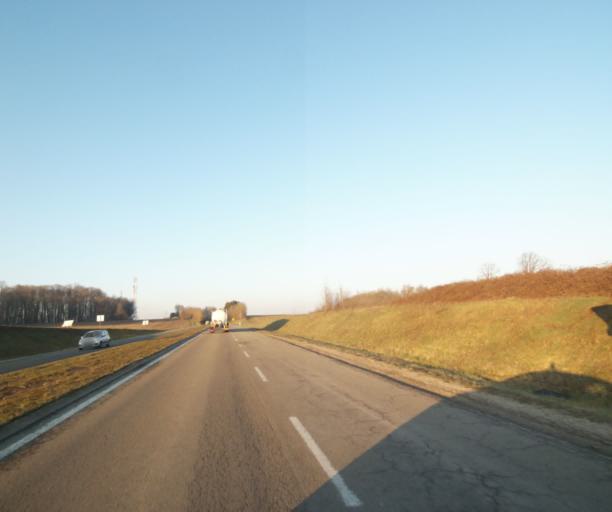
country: FR
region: Champagne-Ardenne
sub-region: Departement de la Haute-Marne
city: Bienville
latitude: 48.5725
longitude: 5.0353
